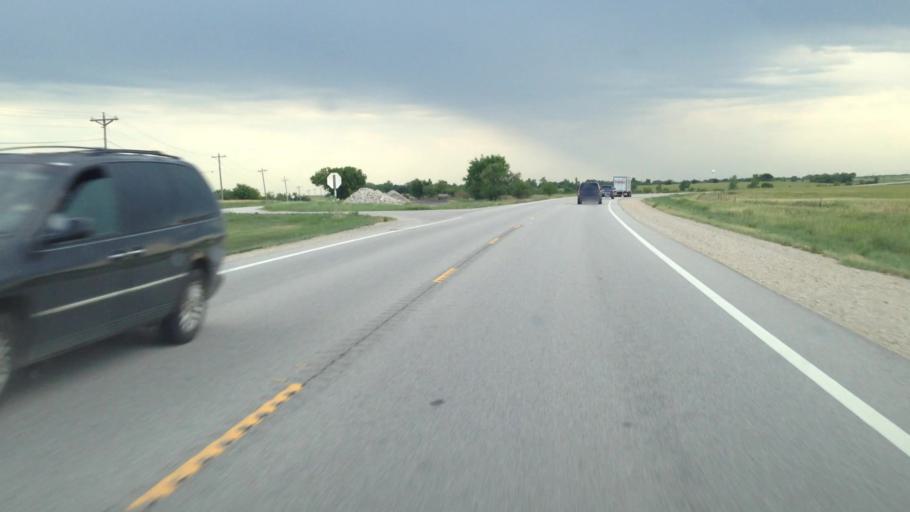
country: US
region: Kansas
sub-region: Coffey County
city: Burlington
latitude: 38.3004
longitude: -95.7289
